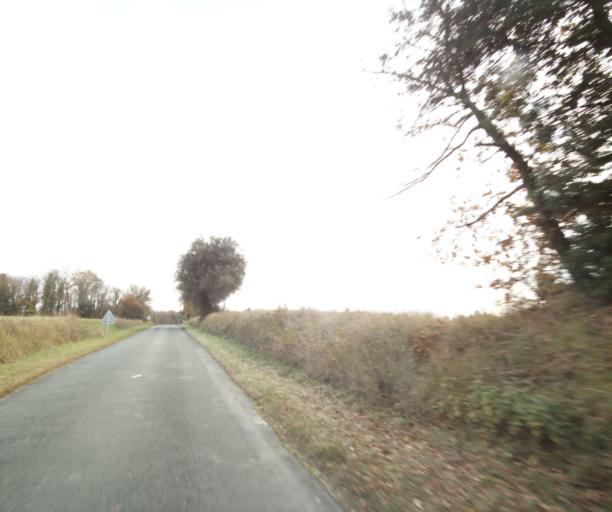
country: FR
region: Poitou-Charentes
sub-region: Departement de la Charente-Maritime
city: Corme-Royal
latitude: 45.7891
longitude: -0.8311
